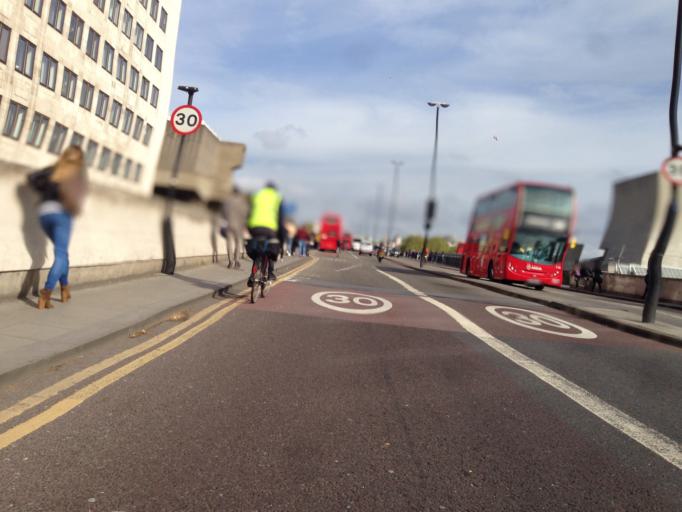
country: GB
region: England
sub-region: Greater London
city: City of Westminster
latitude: 51.5054
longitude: -0.1142
